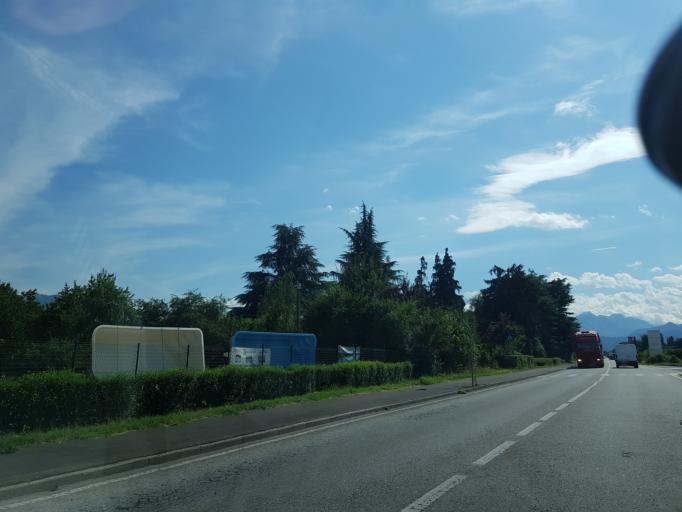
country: IT
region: Piedmont
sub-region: Provincia di Cuneo
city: Cuneo
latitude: 44.4060
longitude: 7.5478
